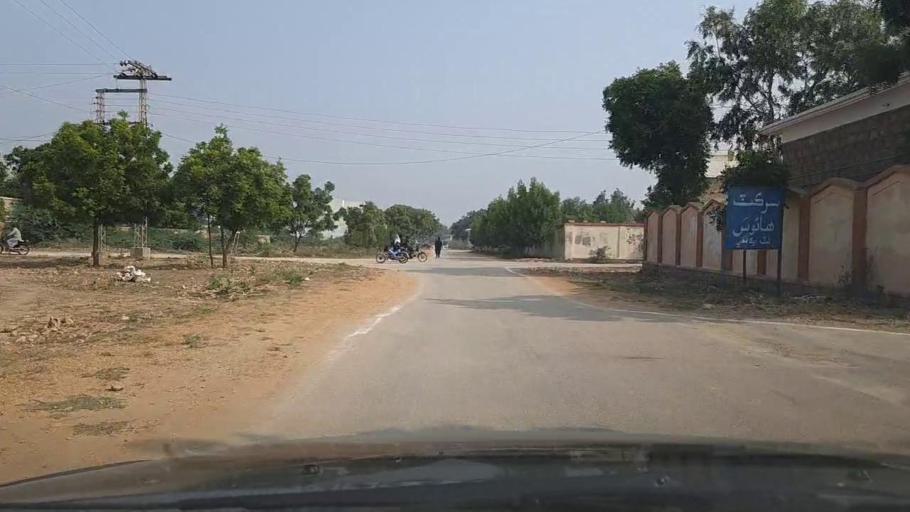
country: PK
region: Sindh
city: Thatta
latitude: 24.7413
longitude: 67.8933
